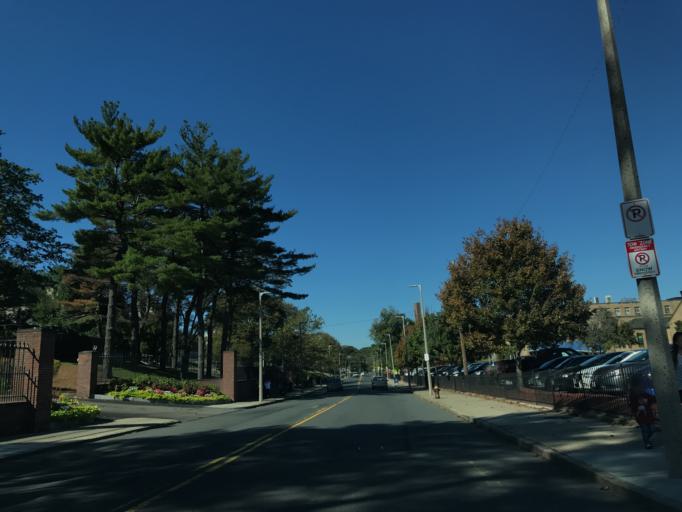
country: US
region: Massachusetts
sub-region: Norfolk County
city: Brookline
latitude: 42.3496
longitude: -71.1432
